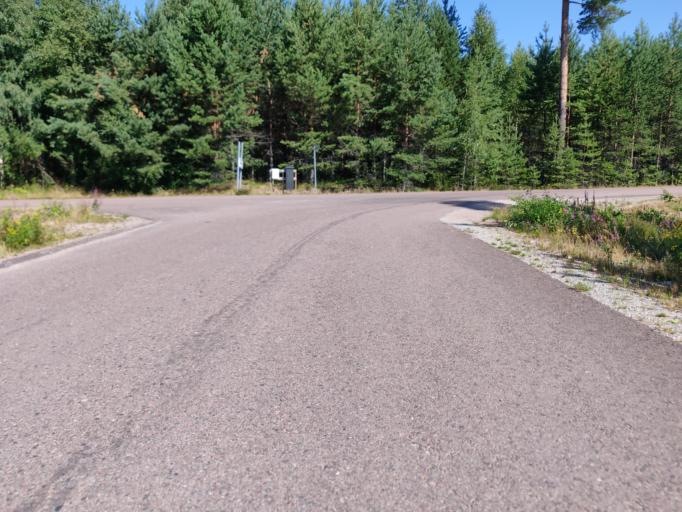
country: SE
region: Vaermland
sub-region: Hagfors Kommun
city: Hagfors
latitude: 60.0260
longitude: 13.5841
